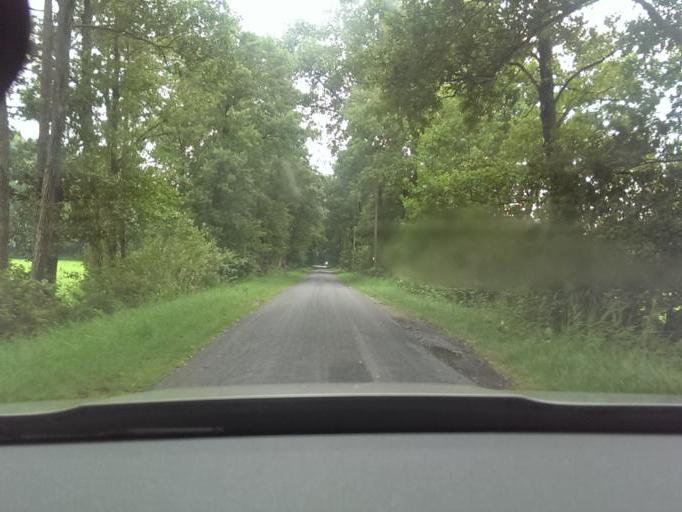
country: DE
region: Lower Saxony
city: Osterholz-Scharmbeck
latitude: 53.1791
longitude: 8.8119
